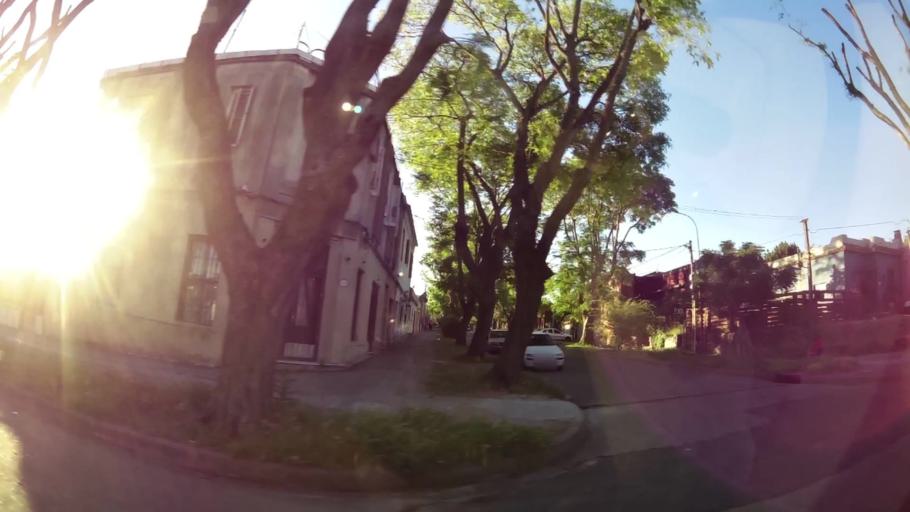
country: UY
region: Montevideo
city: Montevideo
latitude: -34.8503
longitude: -56.2054
